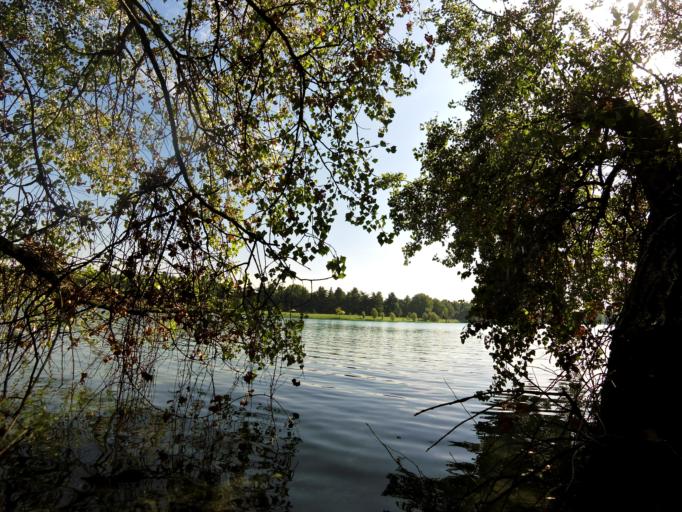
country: IT
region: Lombardy
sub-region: Citta metropolitana di Milano
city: Novegro-Tregarezzo-San Felice
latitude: 45.4584
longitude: 9.2864
